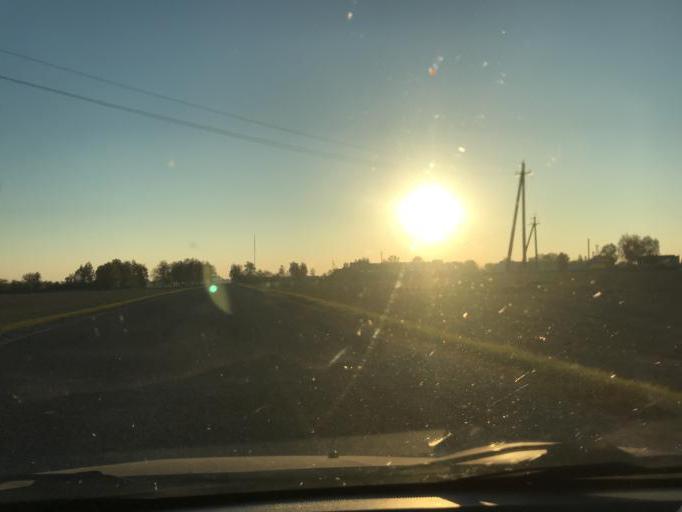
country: BY
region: Gomel
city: Brahin
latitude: 51.8128
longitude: 30.2888
